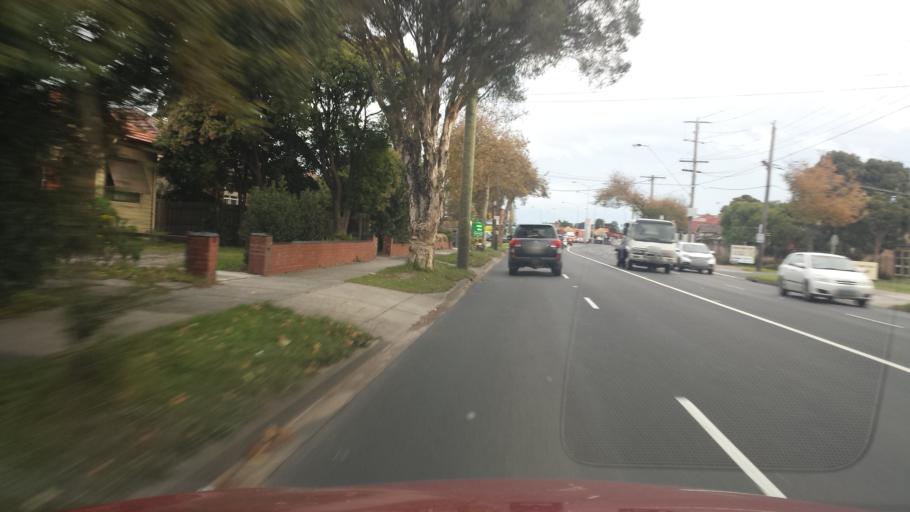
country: AU
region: Victoria
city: Hughesdale
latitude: -37.9070
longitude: 145.0856
